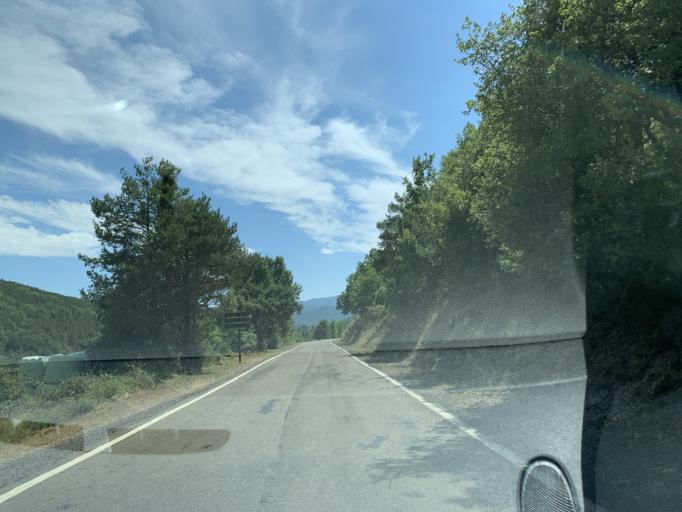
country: ES
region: Aragon
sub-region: Provincia de Huesca
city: Jasa
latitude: 42.6185
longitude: -0.6609
